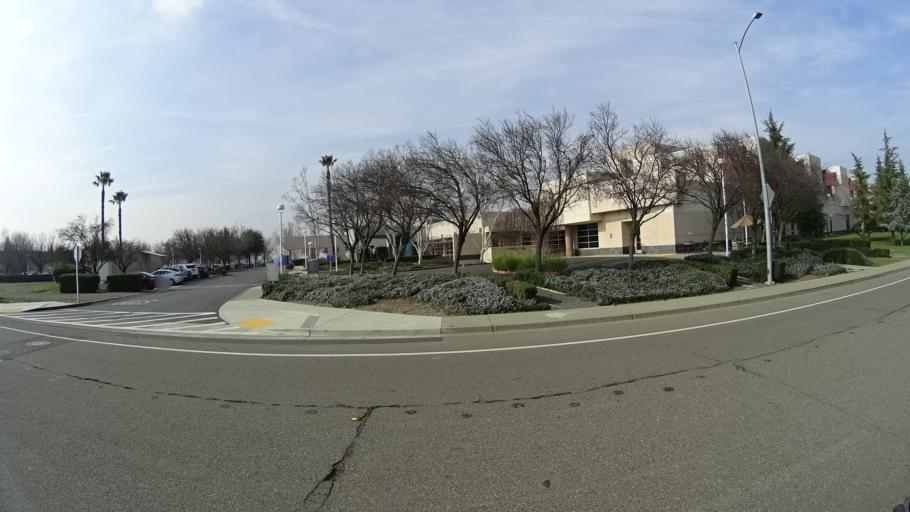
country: US
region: California
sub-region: Yolo County
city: Davis
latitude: 38.5620
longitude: -121.7702
